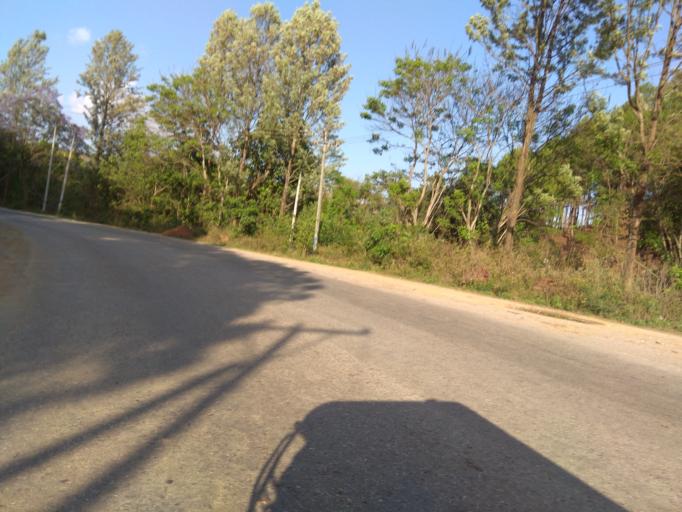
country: MM
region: Shan
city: Taunggyi
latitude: 20.6328
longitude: 96.5853
